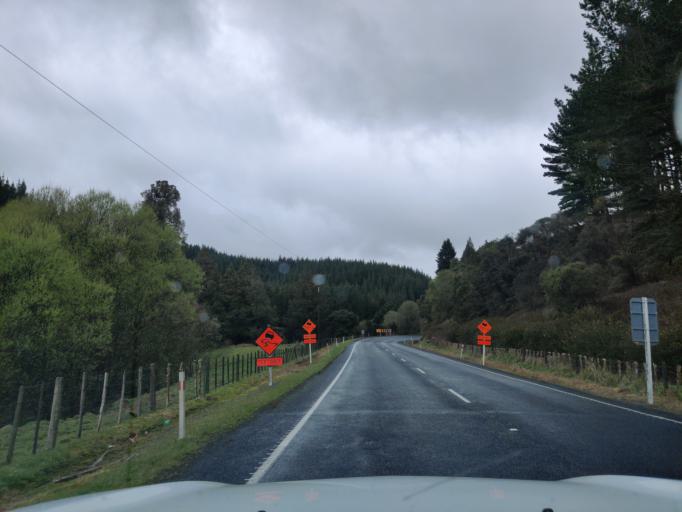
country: NZ
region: Waikato
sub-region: Otorohanga District
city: Otorohanga
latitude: -38.6564
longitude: 175.2083
